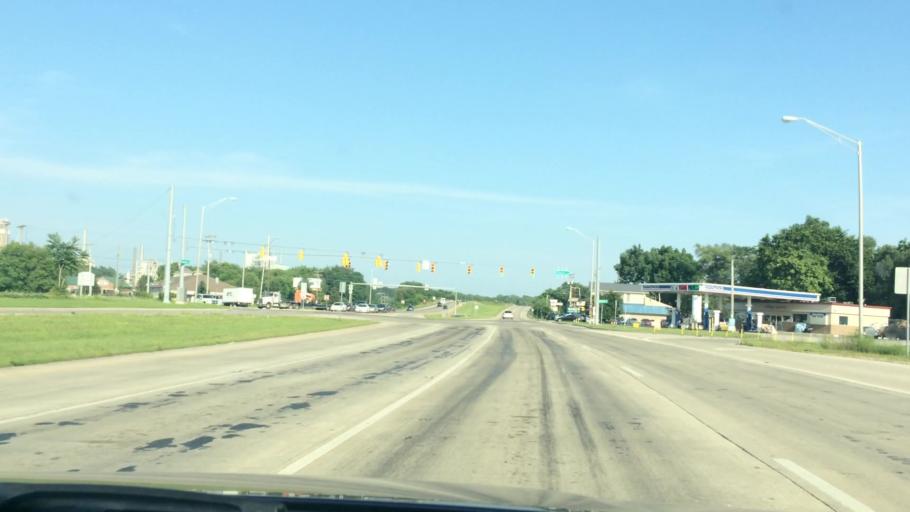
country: US
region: Indiana
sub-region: Tippecanoe County
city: Lafayette
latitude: 40.4441
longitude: -86.8699
